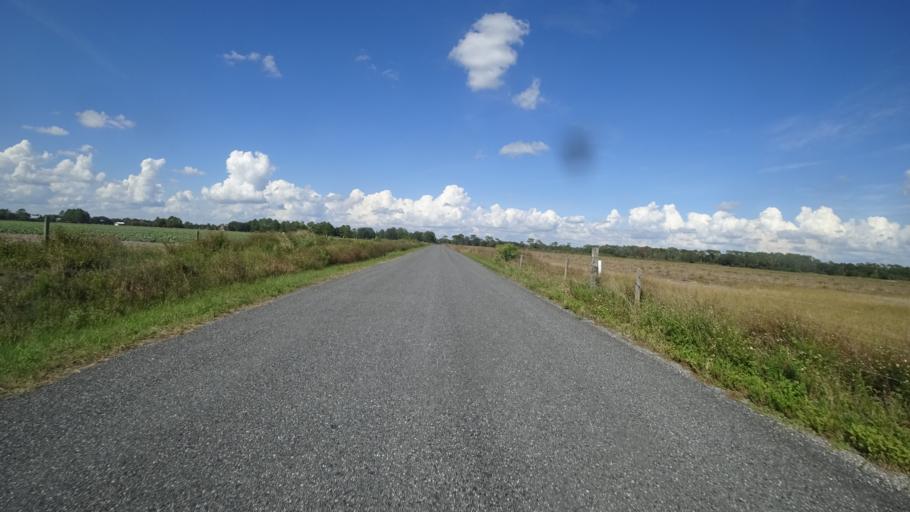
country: US
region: Florida
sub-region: Sarasota County
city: The Meadows
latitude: 27.4377
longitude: -82.2871
